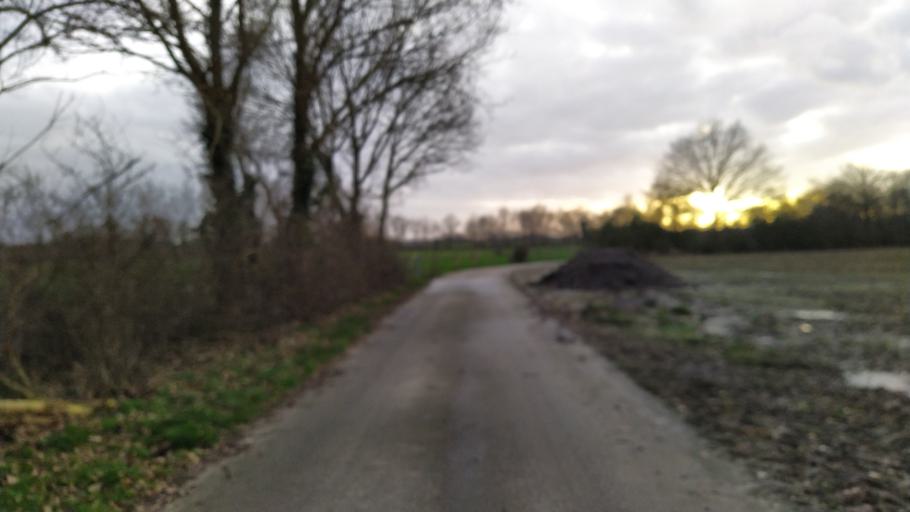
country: DE
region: Lower Saxony
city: Harsefeld
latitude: 53.4401
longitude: 9.4793
